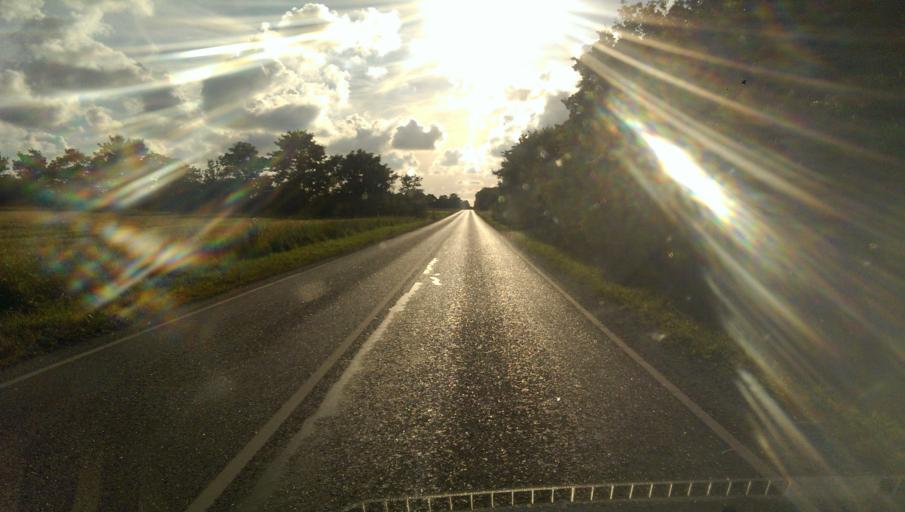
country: DK
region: South Denmark
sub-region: Esbjerg Kommune
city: Esbjerg
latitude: 55.5177
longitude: 8.5106
